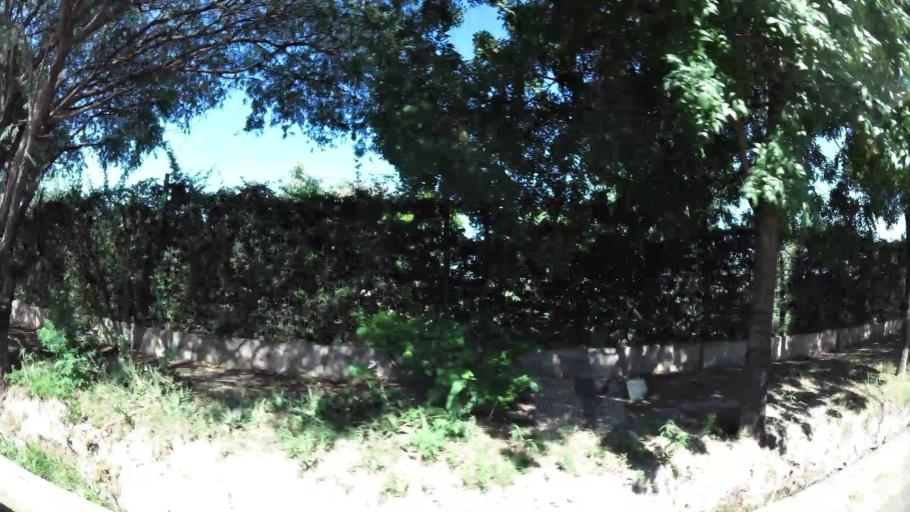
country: AR
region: Mendoza
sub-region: Departamento de Godoy Cruz
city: Godoy Cruz
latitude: -32.9490
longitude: -68.8130
